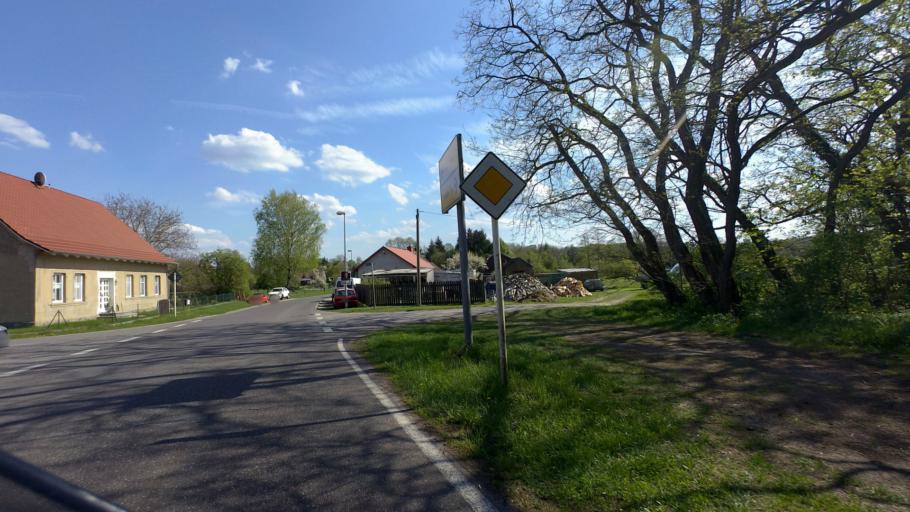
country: DE
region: Brandenburg
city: Templin
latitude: 53.0552
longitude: 13.5260
